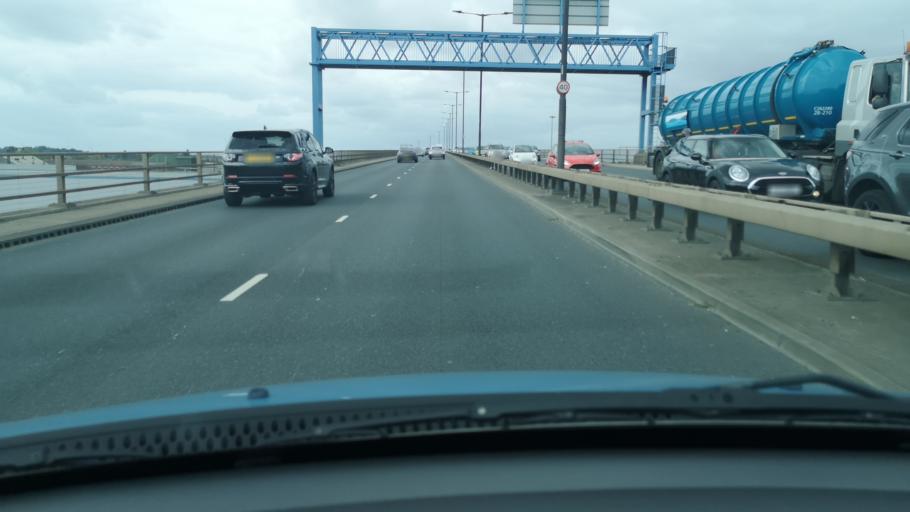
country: GB
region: England
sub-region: Doncaster
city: Doncaster
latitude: 53.5274
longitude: -1.1354
